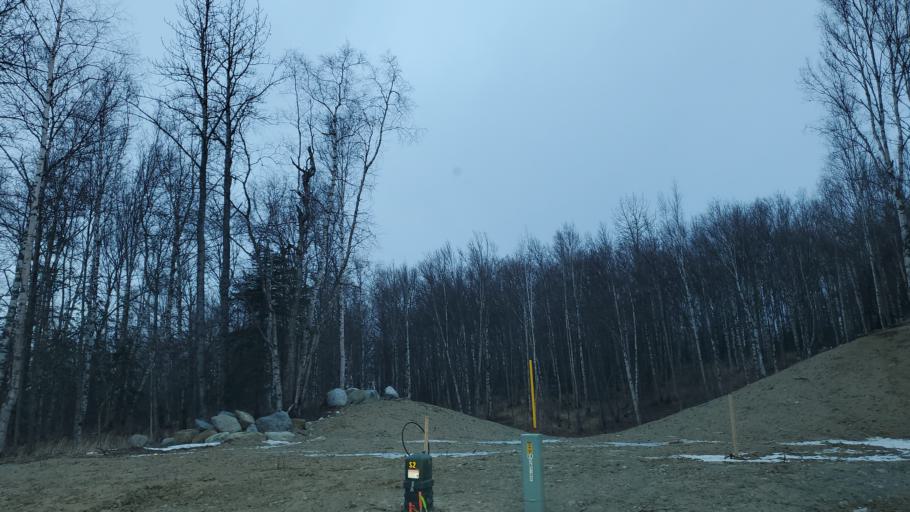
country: US
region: Alaska
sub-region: Matanuska-Susitna Borough
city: Farm Loop
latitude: 61.6563
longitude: -149.2247
